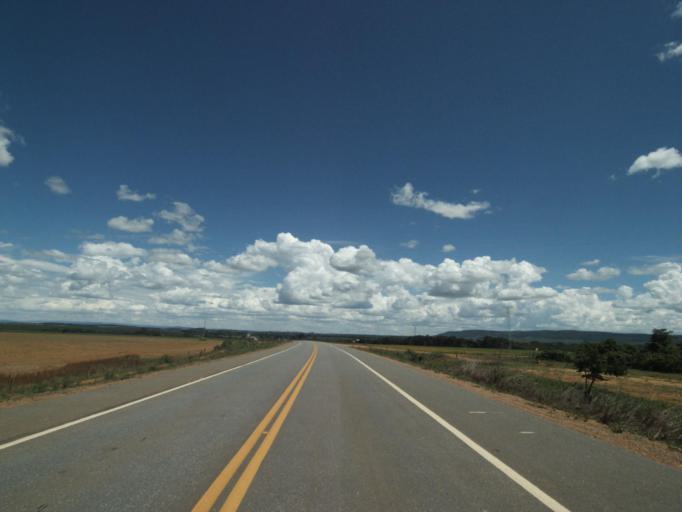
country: BR
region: Goias
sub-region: Barro Alto
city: Barro Alto
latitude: -15.2931
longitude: -48.6765
